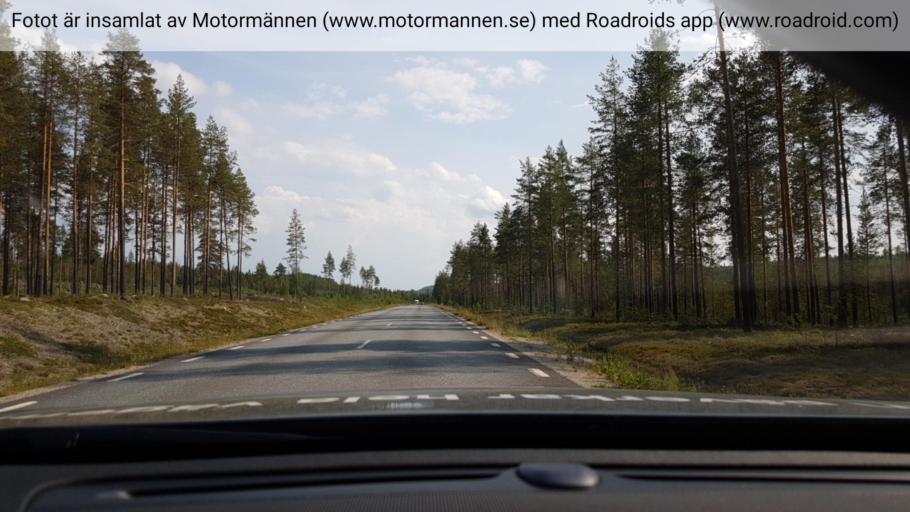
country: SE
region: Vaesterbotten
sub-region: Lycksele Kommun
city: Lycksele
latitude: 64.4149
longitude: 19.0142
